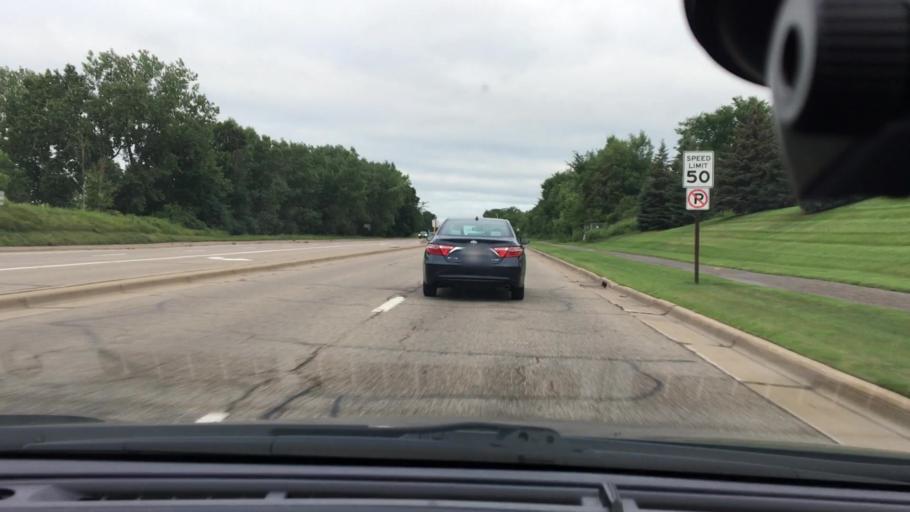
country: US
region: Minnesota
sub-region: Hennepin County
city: New Hope
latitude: 45.0586
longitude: -93.4147
